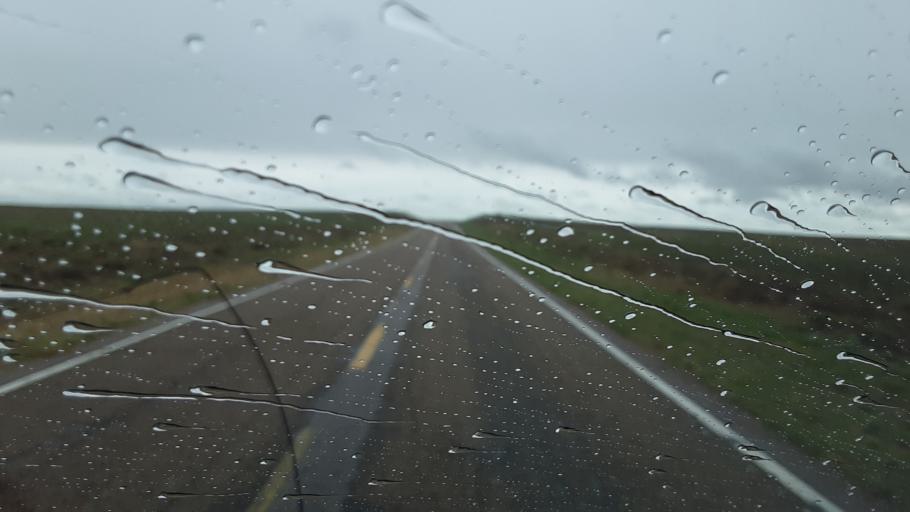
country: US
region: Colorado
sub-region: Lincoln County
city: Hugo
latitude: 38.8494
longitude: -103.2502
